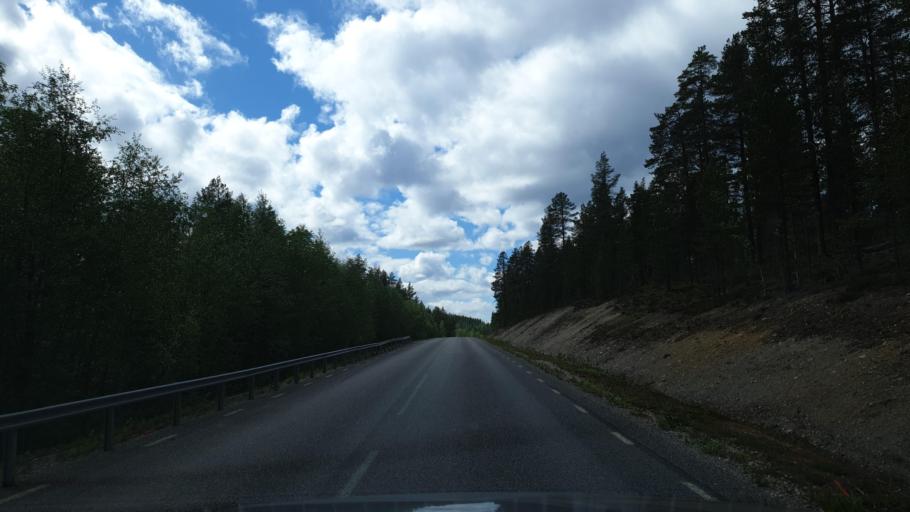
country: SE
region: Norrbotten
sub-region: Jokkmokks Kommun
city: Jokkmokk
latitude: 67.2138
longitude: 19.3189
